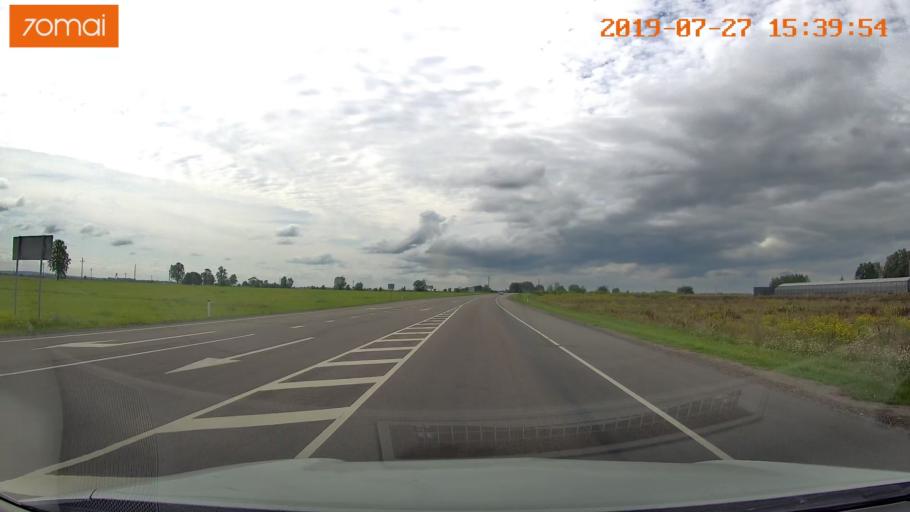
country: RU
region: Kaliningrad
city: Gusev
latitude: 54.6047
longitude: 22.2754
